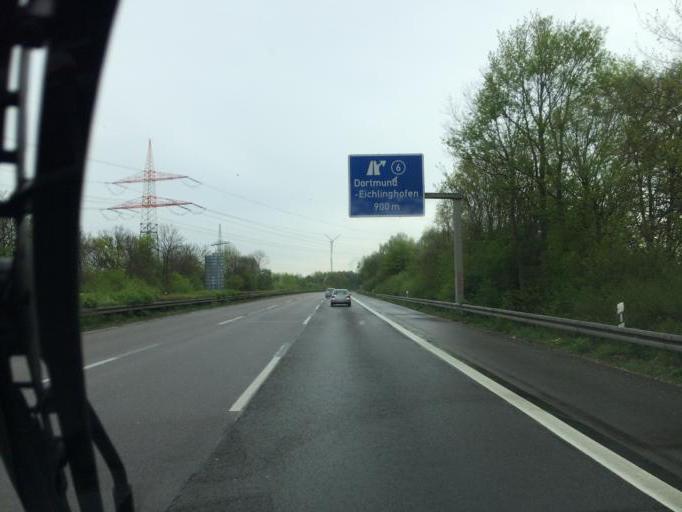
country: DE
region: North Rhine-Westphalia
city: Witten
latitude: 51.4895
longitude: 7.3883
